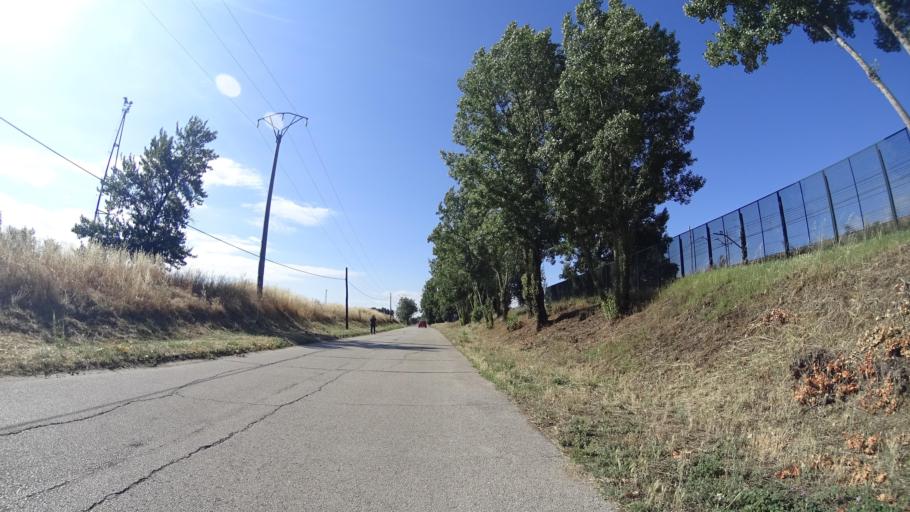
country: ES
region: Madrid
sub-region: Provincia de Madrid
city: Las Matas
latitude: 40.5433
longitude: -3.8917
